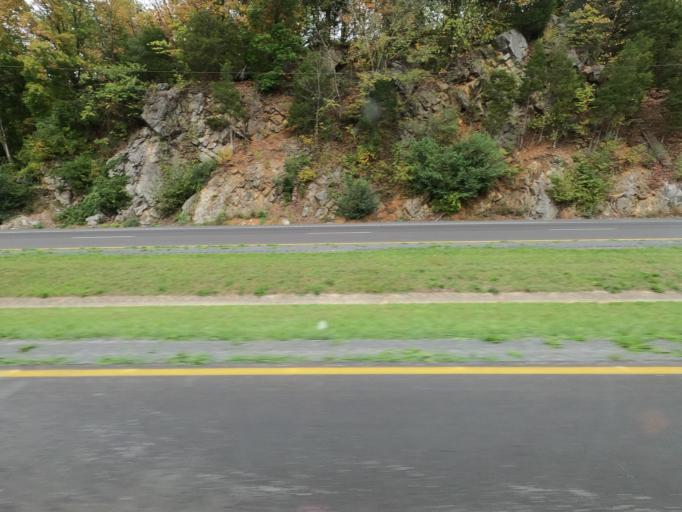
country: US
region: Tennessee
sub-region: Sullivan County
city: Bloomingdale
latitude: 36.5371
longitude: -82.5046
